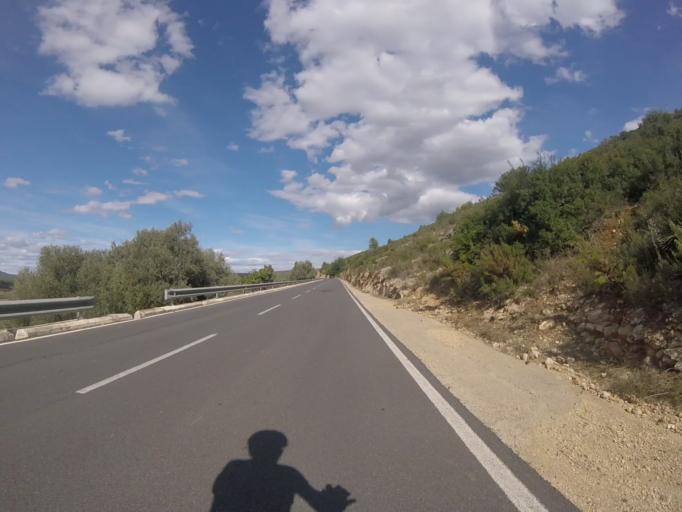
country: ES
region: Valencia
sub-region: Provincia de Castello
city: Cuevas de Vinroma
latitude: 40.3182
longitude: 0.1305
